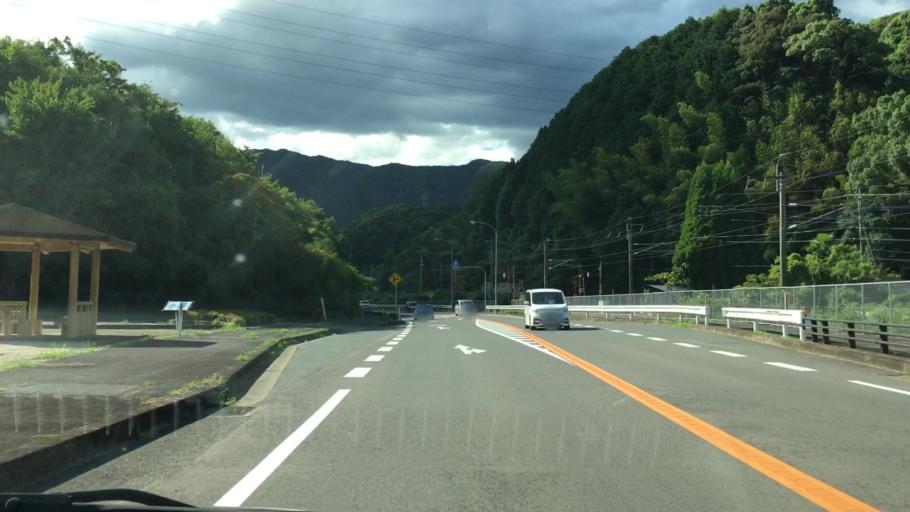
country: JP
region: Saga Prefecture
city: Imaricho-ko
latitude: 33.1896
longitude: 129.9231
